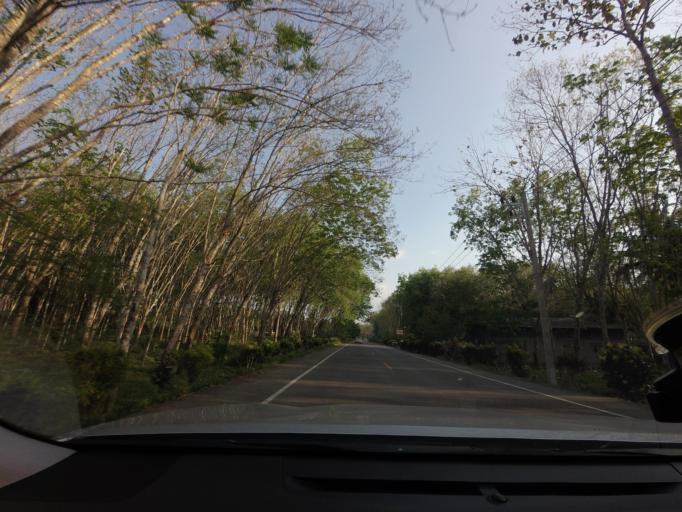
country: TH
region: Surat Thani
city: Phrasaeng
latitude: 8.5757
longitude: 99.2817
